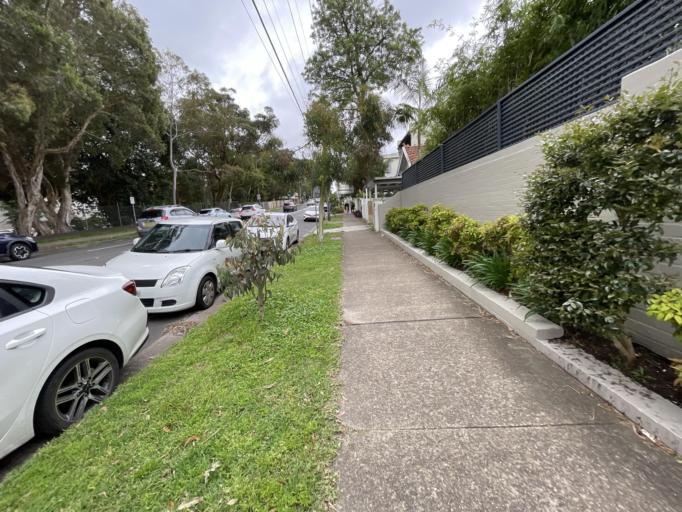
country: AU
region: New South Wales
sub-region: Randwick
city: Randwick
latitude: -33.9207
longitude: 151.2405
